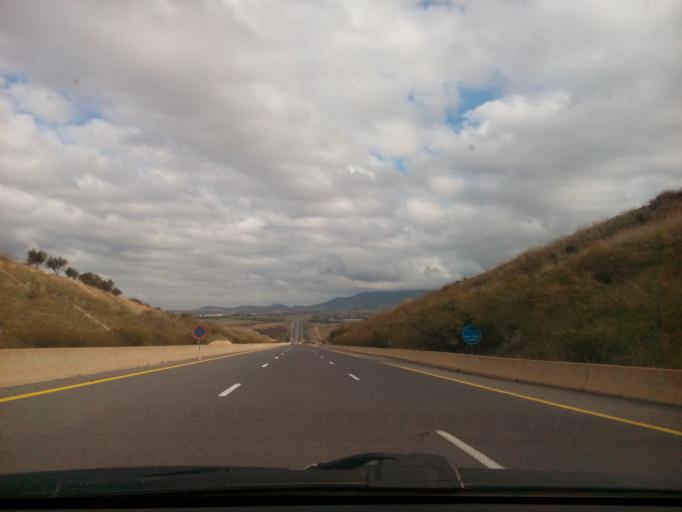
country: DZ
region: Tlemcen
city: Chetouane
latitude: 34.9785
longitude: -1.2518
